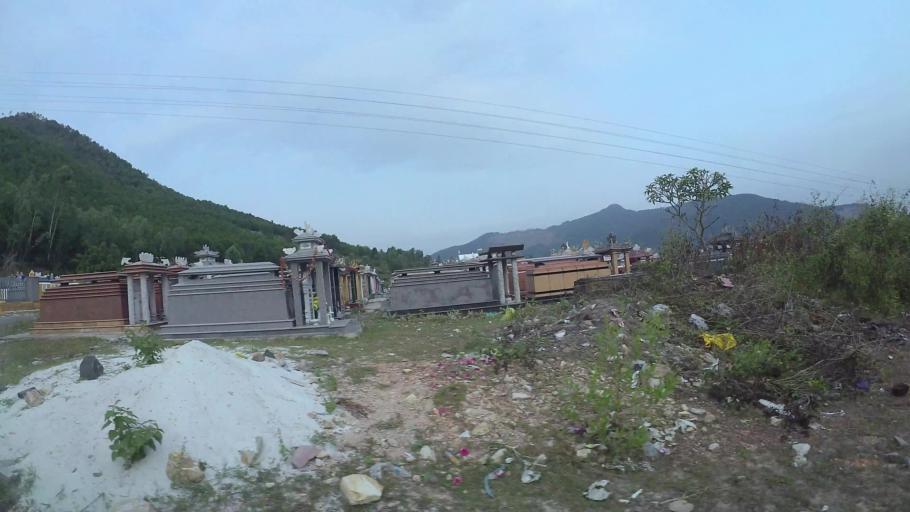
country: VN
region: Da Nang
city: Lien Chieu
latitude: 16.0633
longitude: 108.1095
